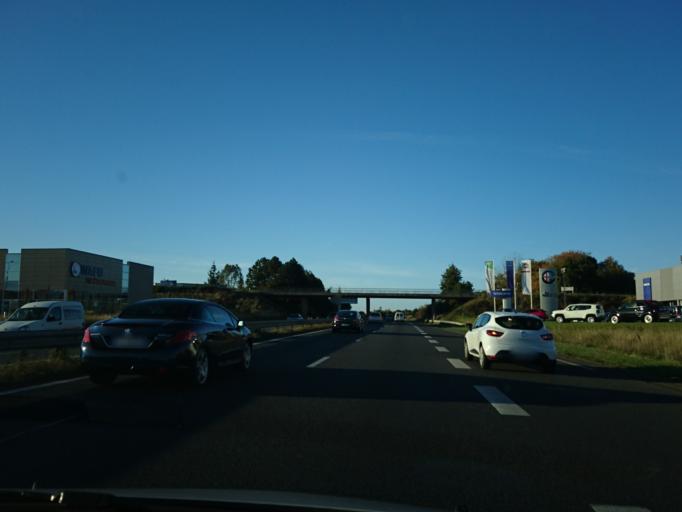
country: FR
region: Brittany
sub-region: Departement des Cotes-d'Armor
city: Plerin
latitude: 48.5365
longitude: -2.7603
